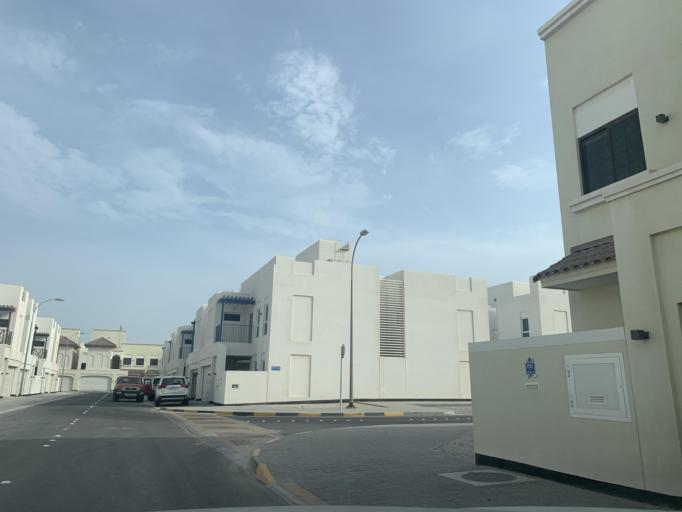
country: BH
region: Muharraq
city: Al Muharraq
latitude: 26.3186
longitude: 50.6298
